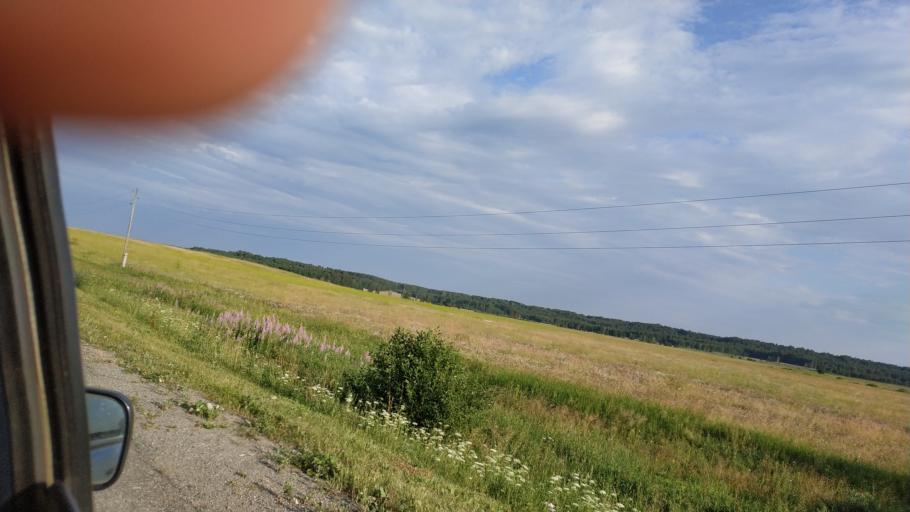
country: RU
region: Sverdlovsk
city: Yelanskiy
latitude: 57.0797
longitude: 62.4946
